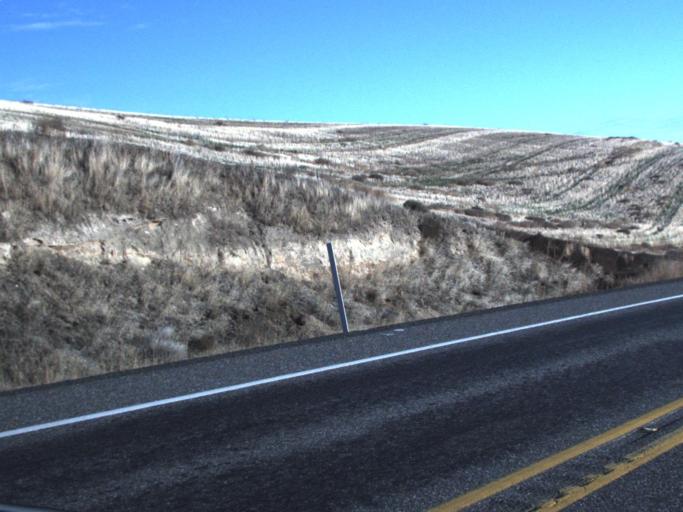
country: US
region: Washington
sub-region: Garfield County
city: Pomeroy
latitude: 46.7248
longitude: -117.7662
